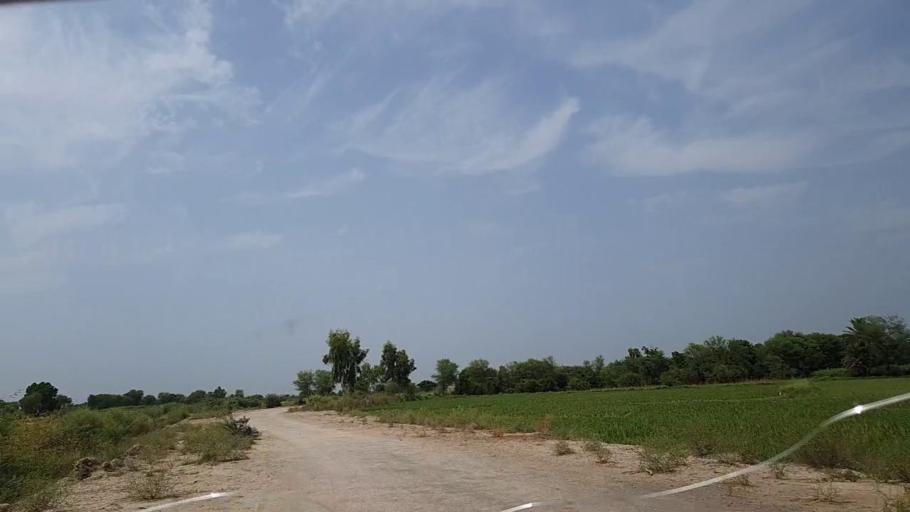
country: PK
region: Sindh
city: Tharu Shah
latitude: 26.9019
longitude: 68.0754
